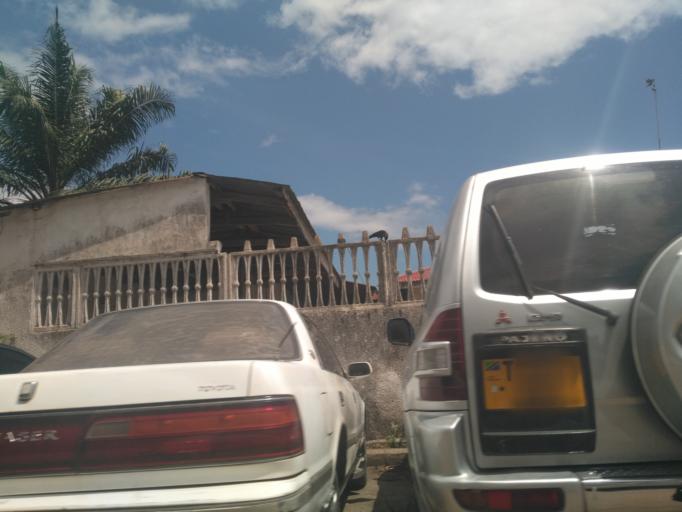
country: TZ
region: Dar es Salaam
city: Magomeni
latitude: -6.7954
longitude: 39.2674
